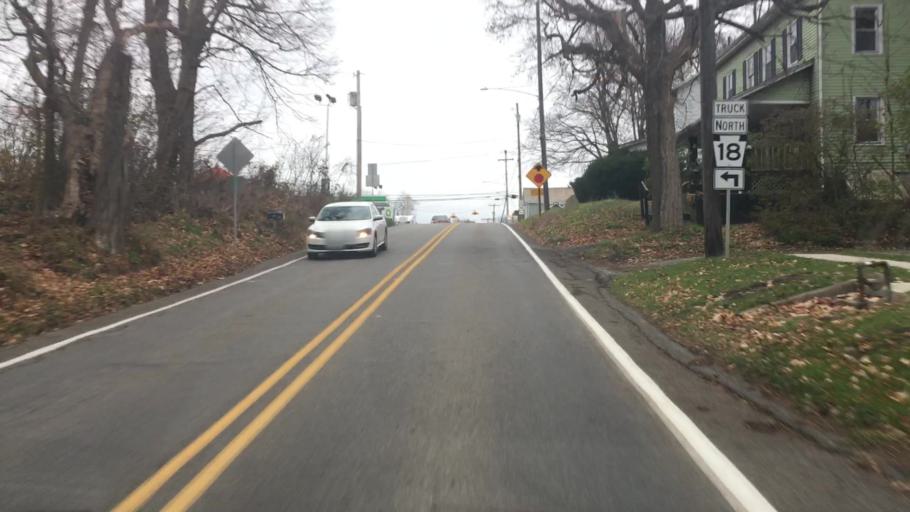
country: US
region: Pennsylvania
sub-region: Lawrence County
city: Bessemer
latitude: 40.9619
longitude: -80.4375
